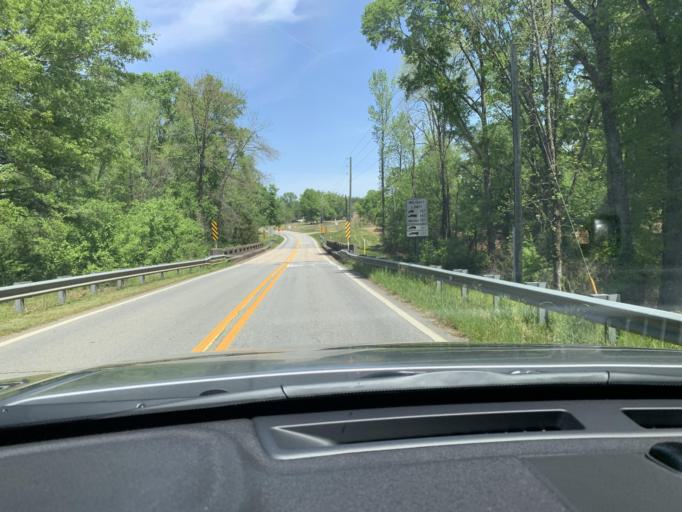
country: US
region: Georgia
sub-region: Oconee County
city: Bogart
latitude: 33.8940
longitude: -83.5033
